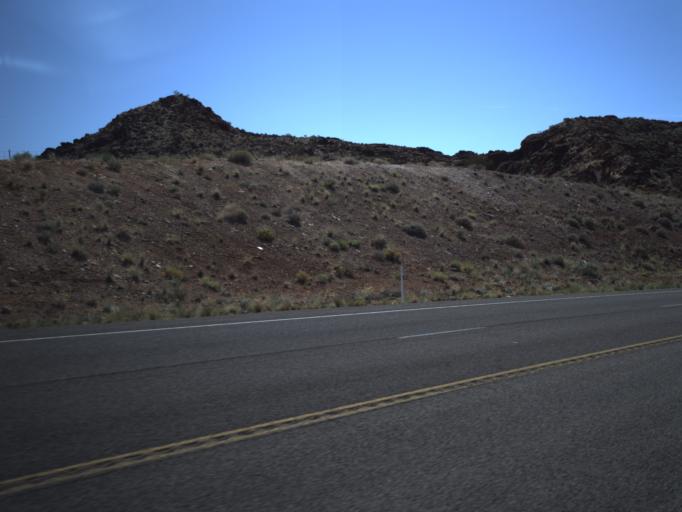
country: US
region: Utah
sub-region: Washington County
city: Saint George
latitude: 37.1563
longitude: -113.6033
